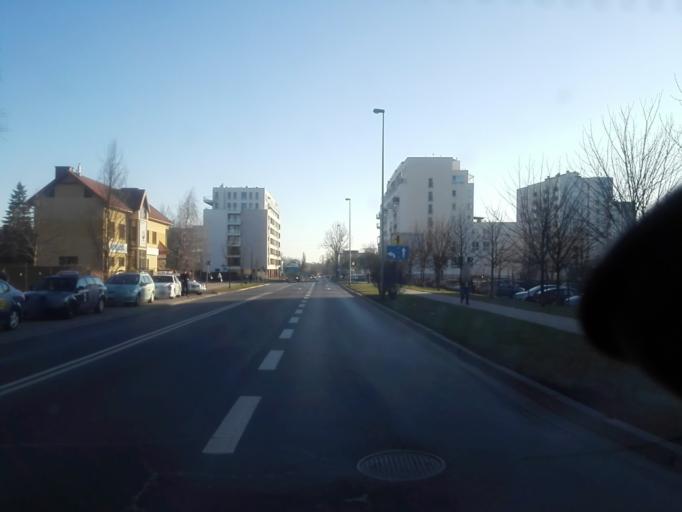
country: PL
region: Masovian Voivodeship
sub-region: Warszawa
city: Mokotow
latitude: 52.1735
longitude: 21.0119
